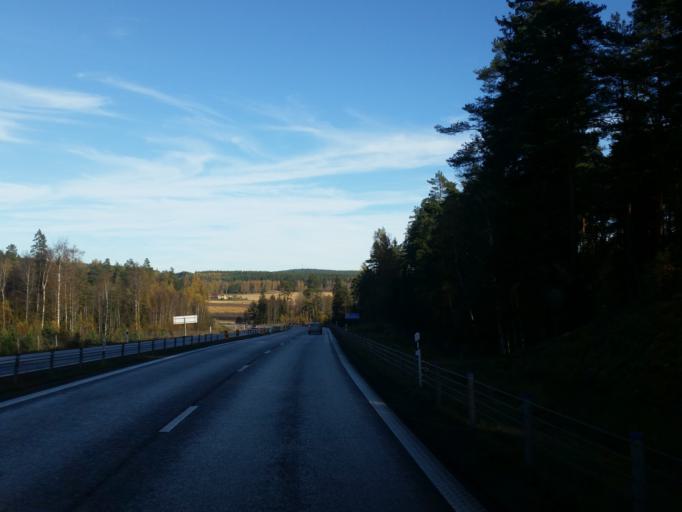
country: SE
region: Dalarna
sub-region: Borlange Kommun
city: Ornas
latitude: 60.5384
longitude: 15.5583
